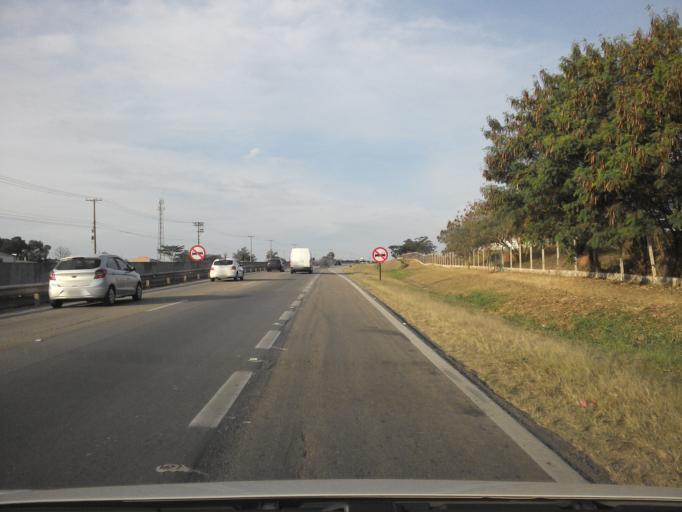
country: BR
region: Sao Paulo
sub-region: Hortolandia
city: Hortolandia
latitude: -22.8878
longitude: -47.1619
